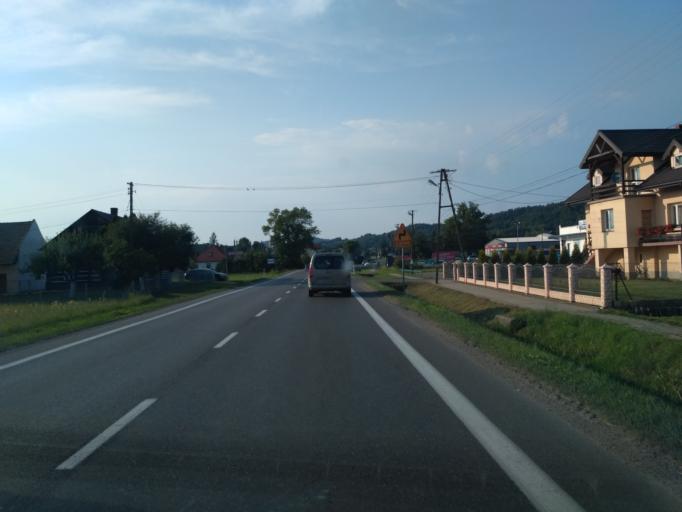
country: PL
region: Subcarpathian Voivodeship
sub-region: Powiat brzozowski
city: Stara Wies
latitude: 49.7163
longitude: 22.0117
